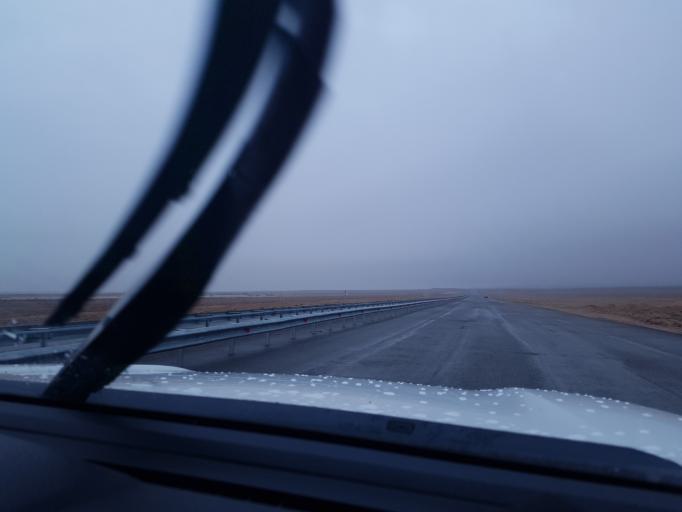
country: TM
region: Balkan
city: Balkanabat
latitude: 39.9628
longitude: 53.8180
